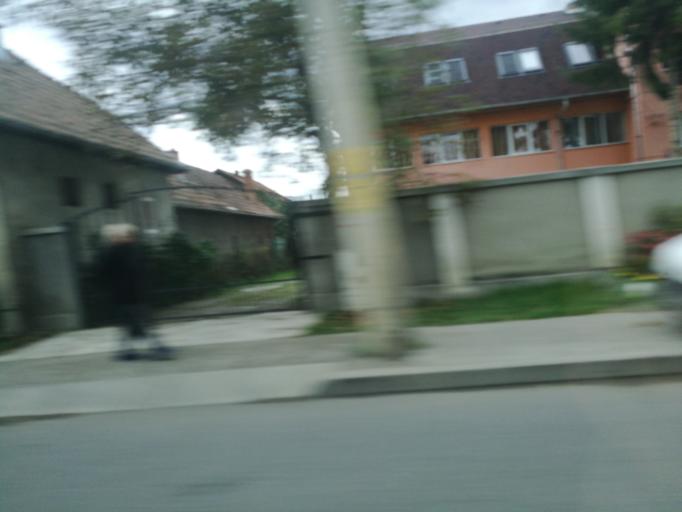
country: RO
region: Mures
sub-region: Comuna Sangeorgiu de Mures
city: Sangeorgiu de Mures
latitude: 46.5714
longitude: 24.5968
